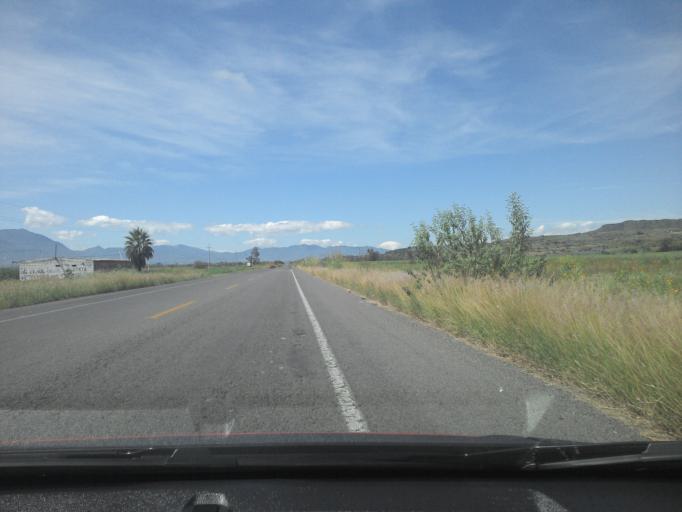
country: MX
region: Jalisco
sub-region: Teuchitlan
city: La Estanzuela
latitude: 20.6694
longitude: -103.8000
